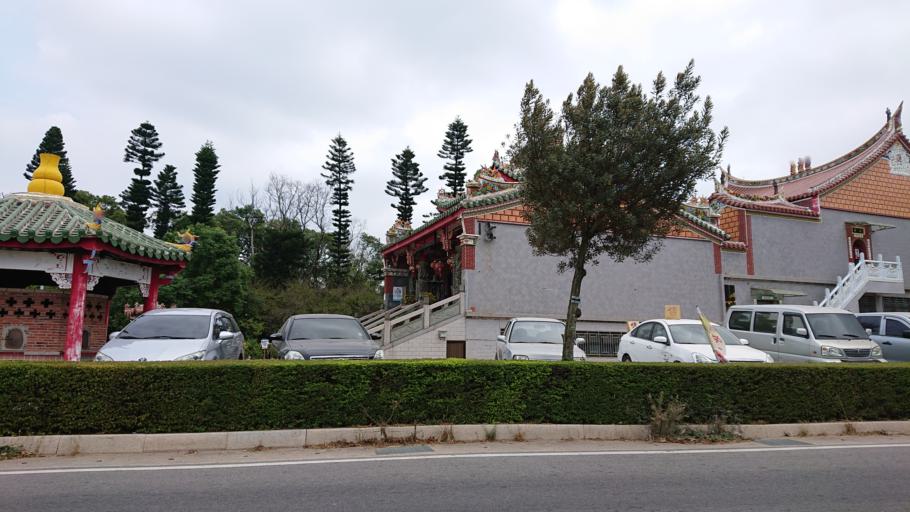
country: TW
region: Fukien
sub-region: Kinmen
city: Jincheng
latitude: 24.4259
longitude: 118.3156
